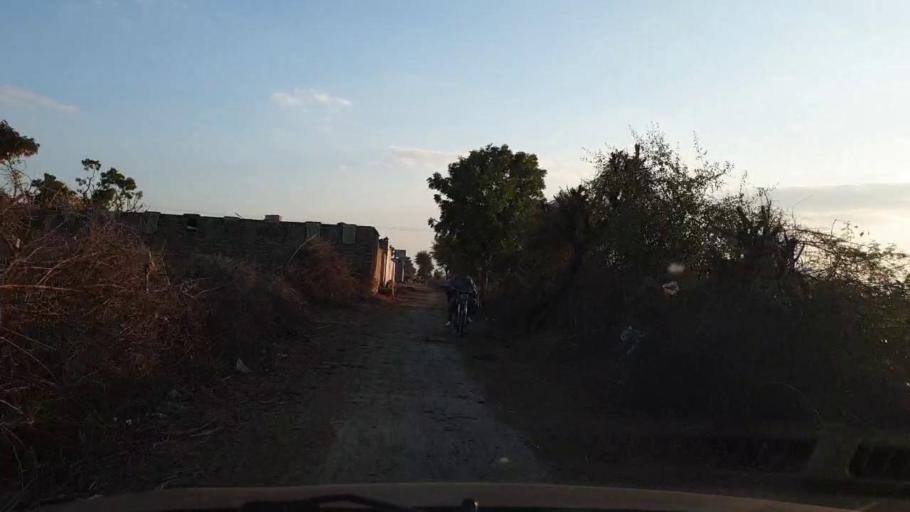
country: PK
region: Sindh
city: Sinjhoro
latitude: 25.9965
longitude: 68.8014
